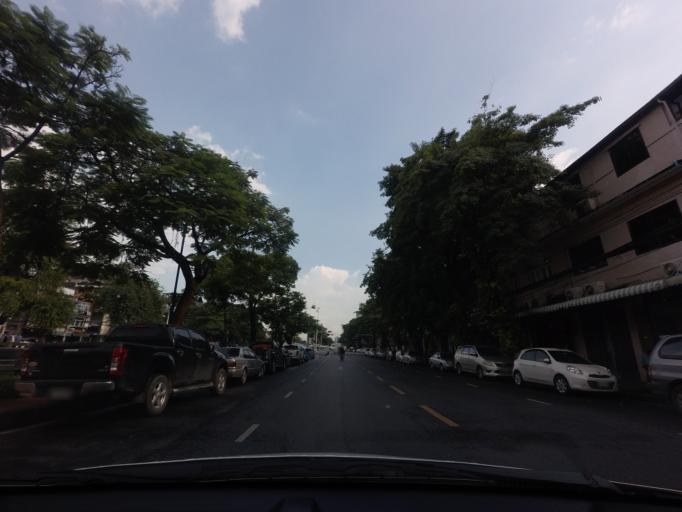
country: TH
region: Bangkok
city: Pom Prap Sattru Phai
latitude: 13.7607
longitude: 100.5121
